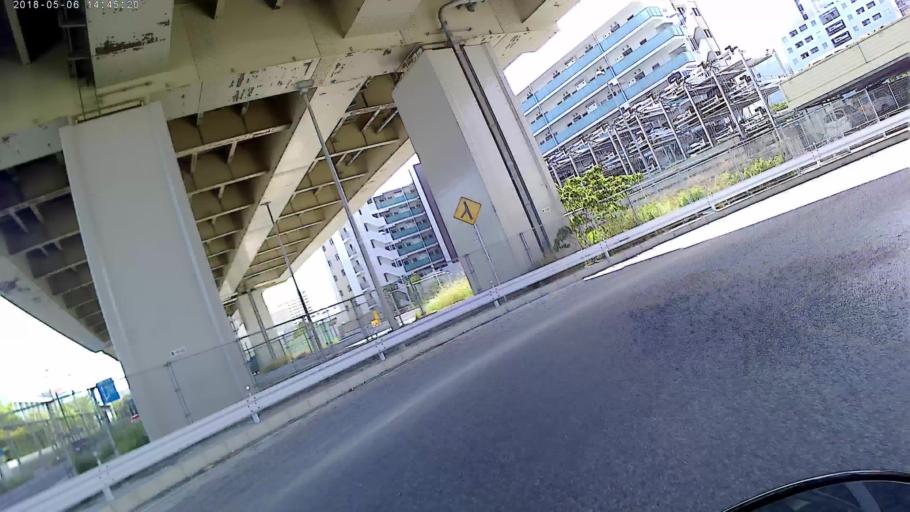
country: JP
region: Kanagawa
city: Yokohama
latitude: 35.4027
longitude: 139.6210
